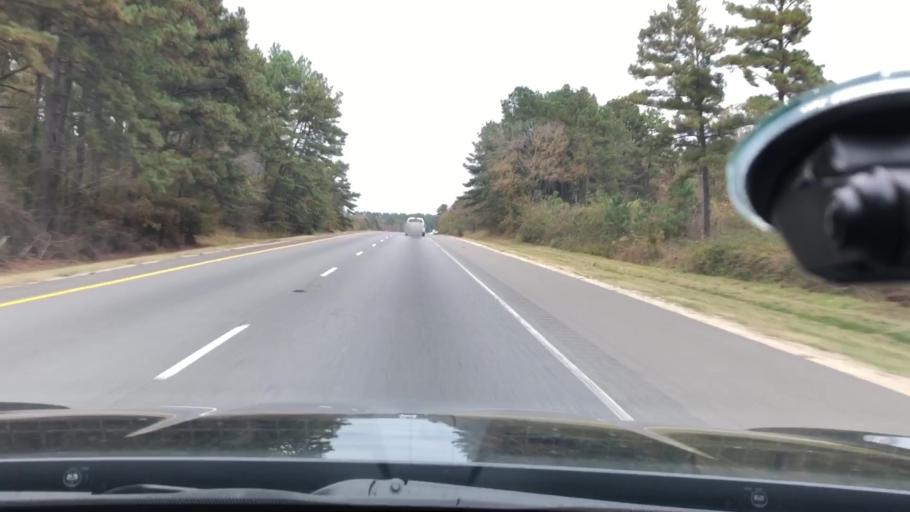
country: US
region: Arkansas
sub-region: Hot Spring County
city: Malvern
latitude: 34.3103
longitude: -92.9388
